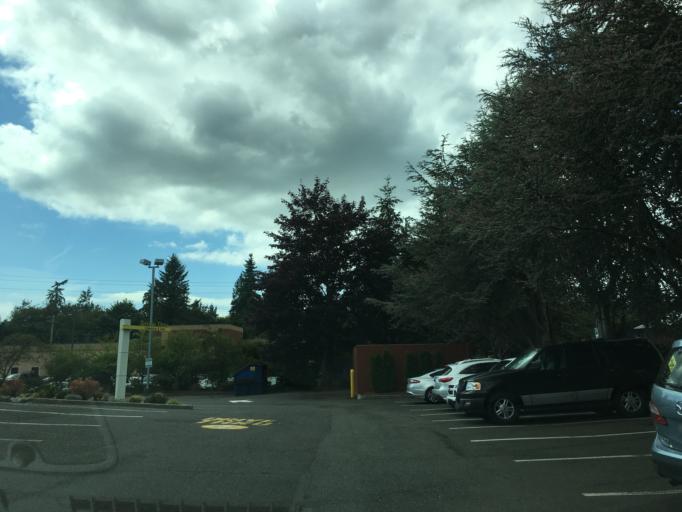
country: US
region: Washington
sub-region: Snohomish County
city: Marysville
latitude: 48.0840
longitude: -122.1734
